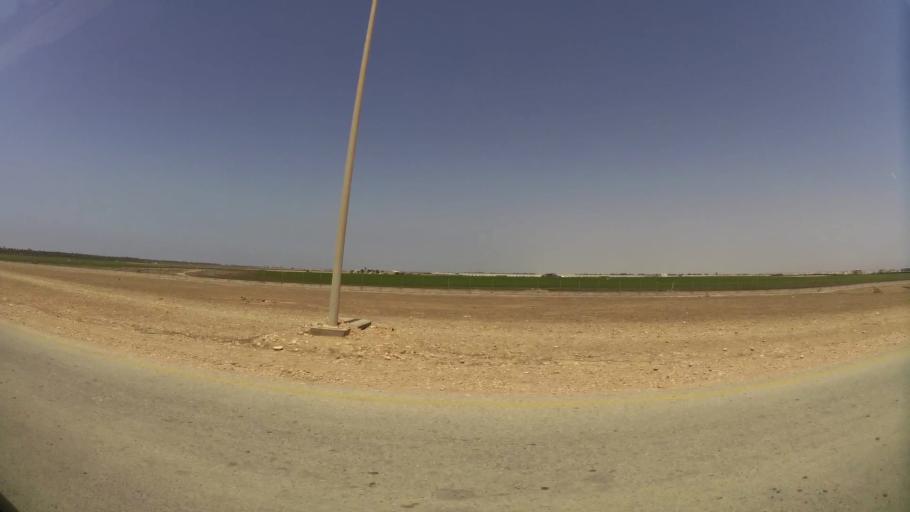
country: OM
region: Zufar
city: Salalah
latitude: 17.0528
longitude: 54.2022
